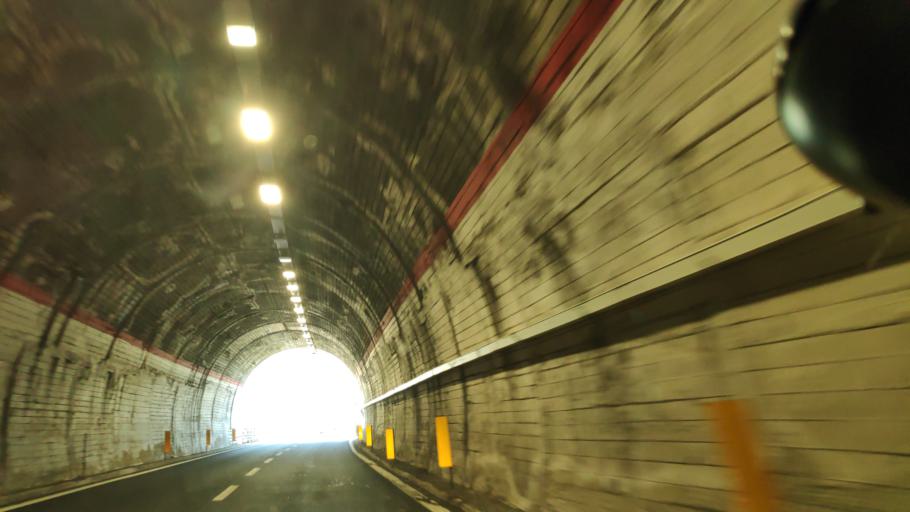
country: IT
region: Calabria
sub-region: Provincia di Cosenza
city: Laurignano
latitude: 39.2607
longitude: 16.2527
